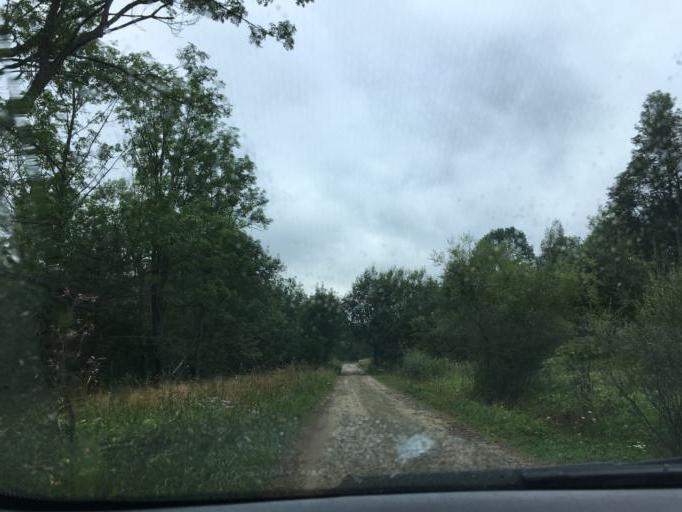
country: PL
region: Subcarpathian Voivodeship
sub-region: Powiat bieszczadzki
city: Lutowiska
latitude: 49.1585
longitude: 22.6303
